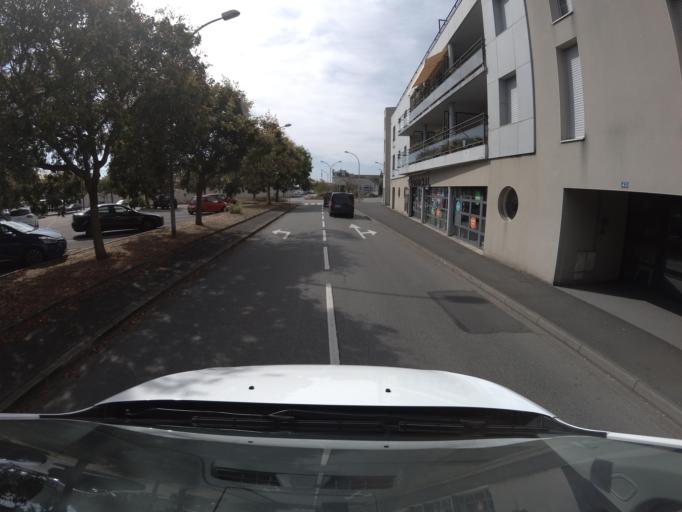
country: FR
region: Poitou-Charentes
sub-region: Departement des Deux-Sevres
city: Thouars
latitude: 46.9787
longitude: -0.2117
